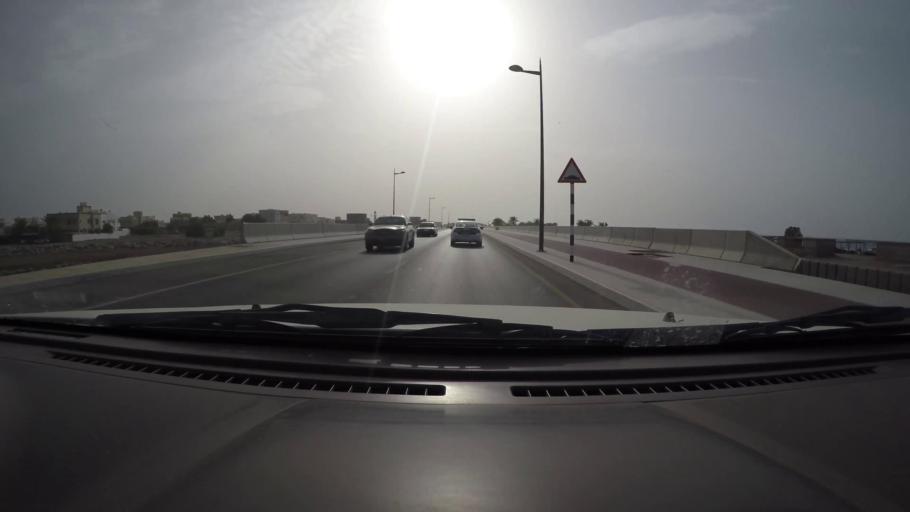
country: OM
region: Muhafazat Masqat
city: As Sib al Jadidah
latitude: 23.6969
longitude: 58.1510
